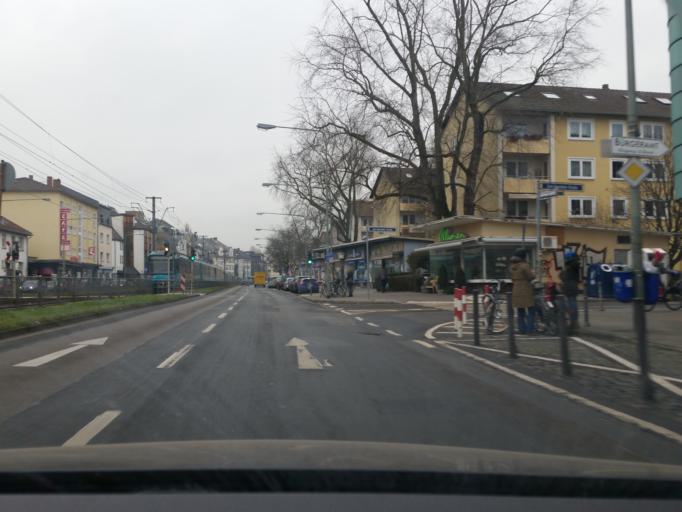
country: DE
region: Hesse
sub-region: Regierungsbezirk Darmstadt
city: Frankfurt am Main
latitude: 50.1397
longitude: 8.6703
